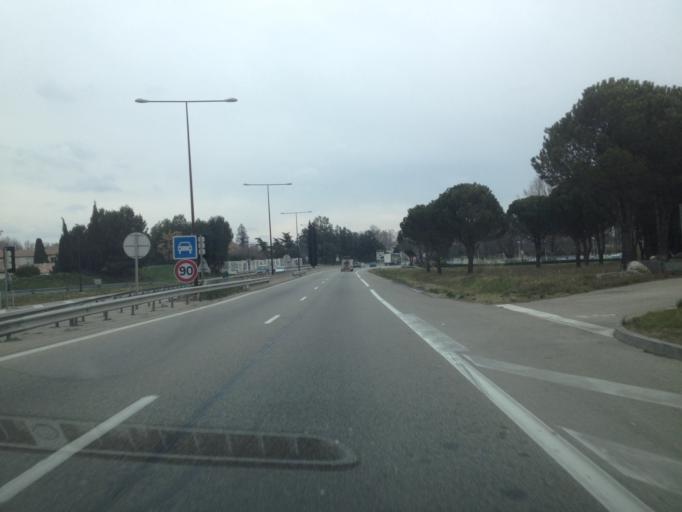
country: FR
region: Provence-Alpes-Cote d'Azur
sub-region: Departement du Vaucluse
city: Avignon
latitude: 43.9415
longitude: 4.8327
